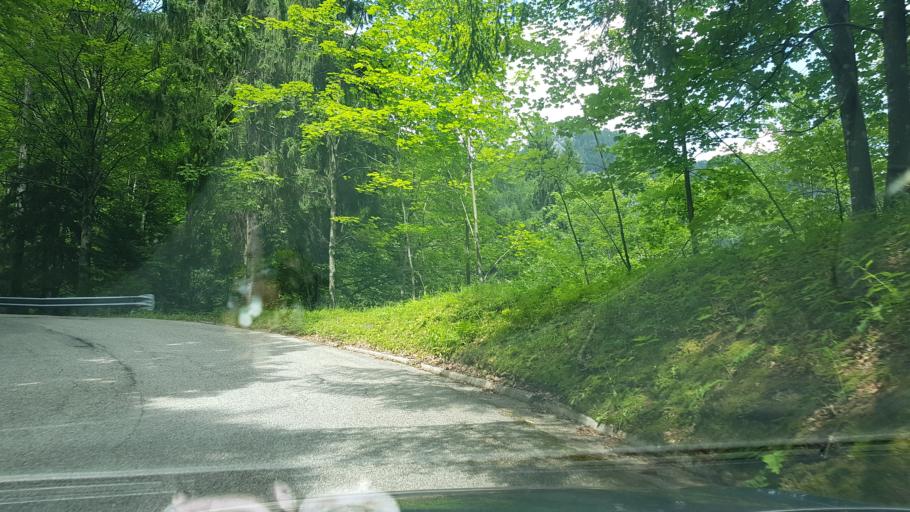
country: IT
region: Friuli Venezia Giulia
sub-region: Provincia di Udine
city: Pontebba
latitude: 46.5030
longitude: 13.2509
